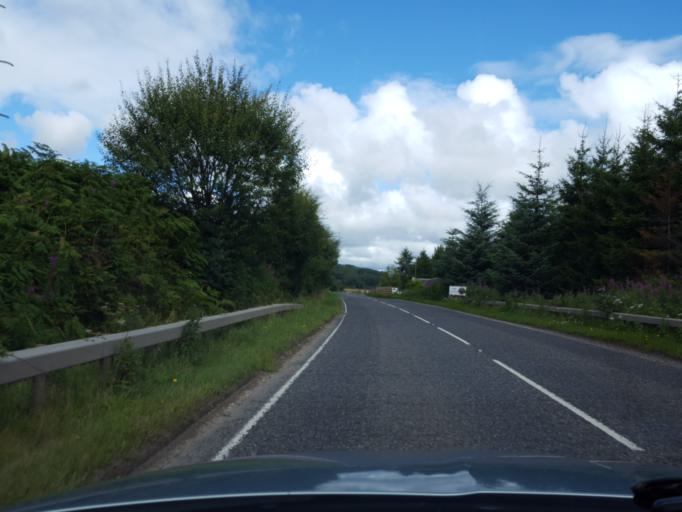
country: GB
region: Scotland
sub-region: Moray
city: Rothes
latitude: 57.5454
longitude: -3.2331
